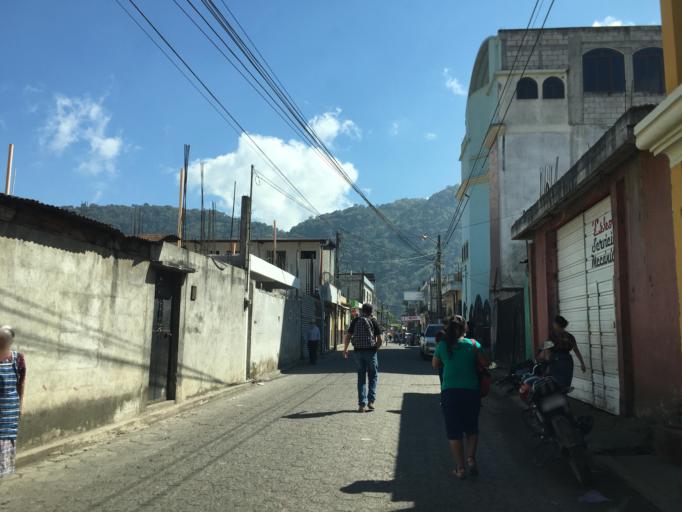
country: GT
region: Solola
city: San Lucas Toliman
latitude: 14.6358
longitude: -91.1443
